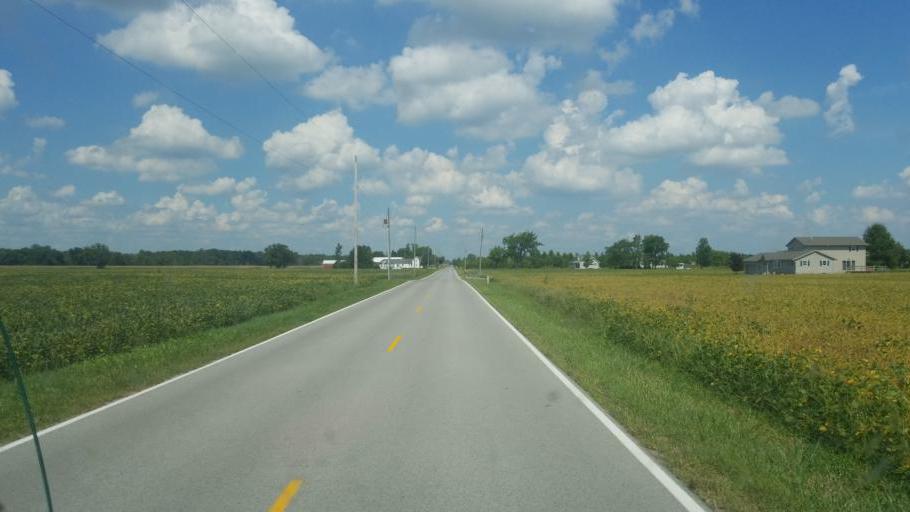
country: US
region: Ohio
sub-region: Hancock County
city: Arlington
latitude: 40.8785
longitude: -83.7272
